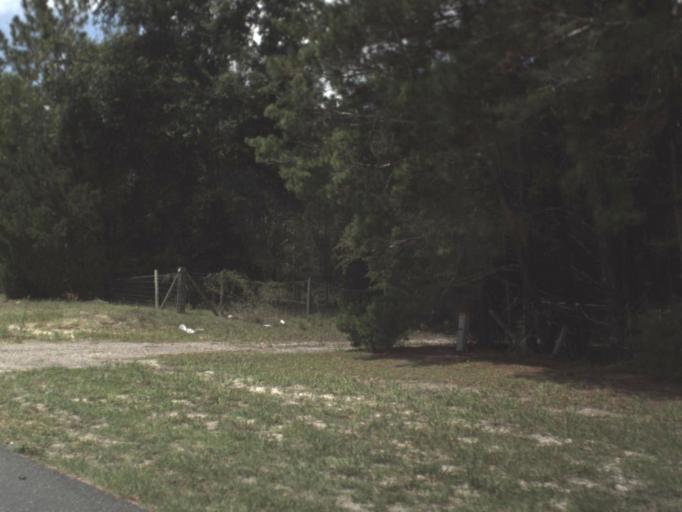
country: US
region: Florida
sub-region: Gilchrist County
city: Trenton
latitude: 29.7781
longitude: -82.8667
